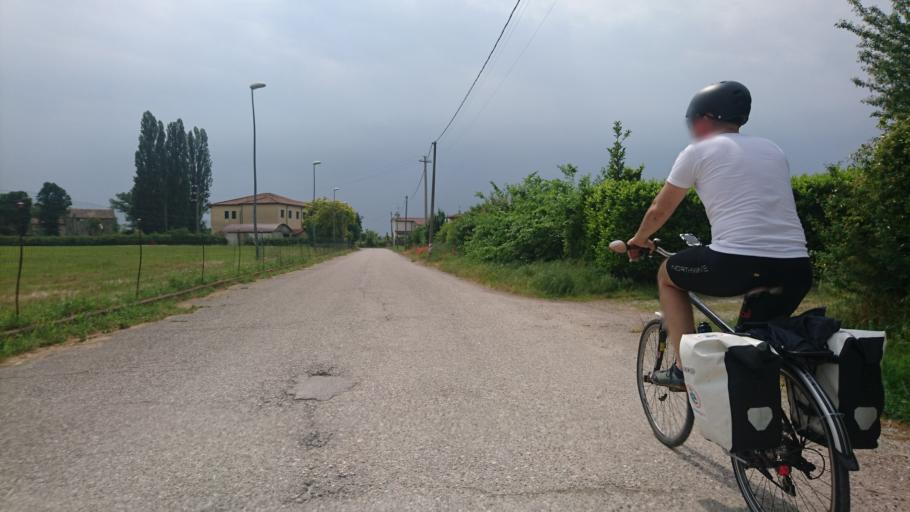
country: IT
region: Veneto
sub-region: Provincia di Padova
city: Monselice
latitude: 45.2157
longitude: 11.7326
